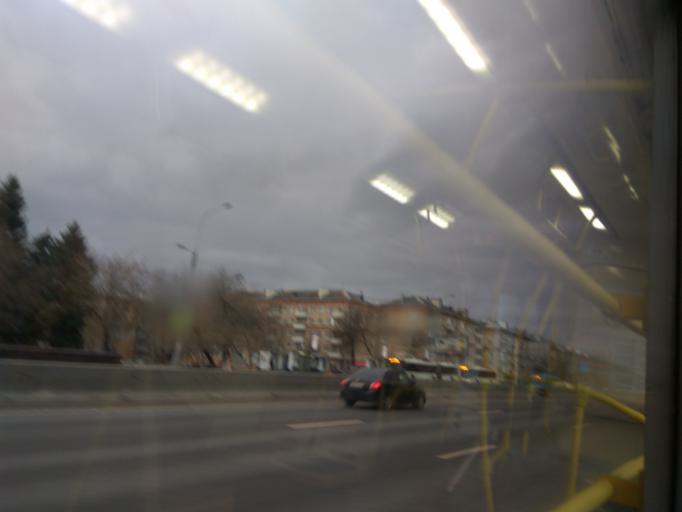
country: RU
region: Moscow
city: Kolomenskoye
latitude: 55.6470
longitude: 37.6692
